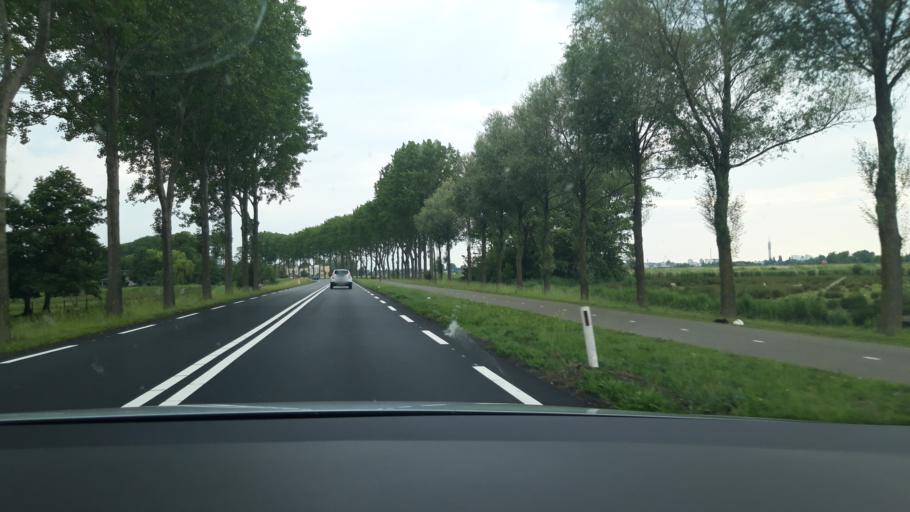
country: NL
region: North Holland
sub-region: Gemeente Zaanstad
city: Zaanstad
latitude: 52.4736
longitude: 4.8337
